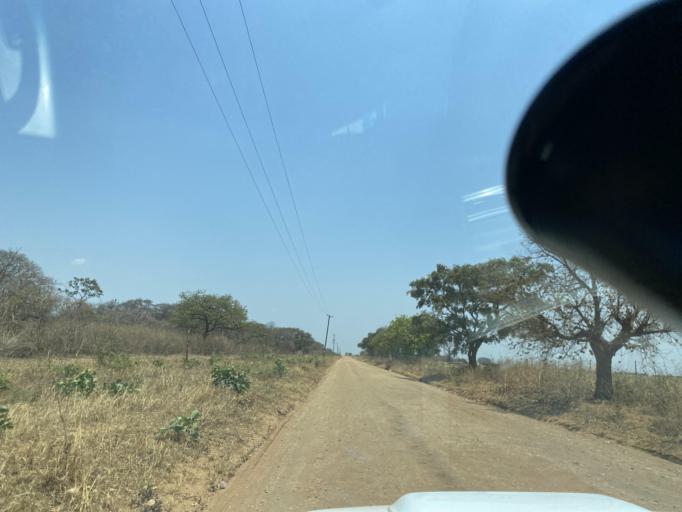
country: ZM
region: Lusaka
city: Lusaka
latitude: -15.4343
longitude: 28.0785
